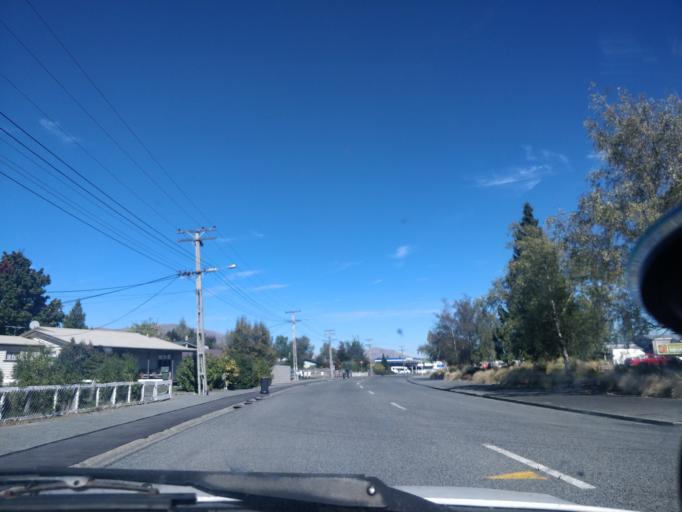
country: NZ
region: Canterbury
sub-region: Timaru District
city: Pleasant Point
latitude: -44.2560
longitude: 170.1011
